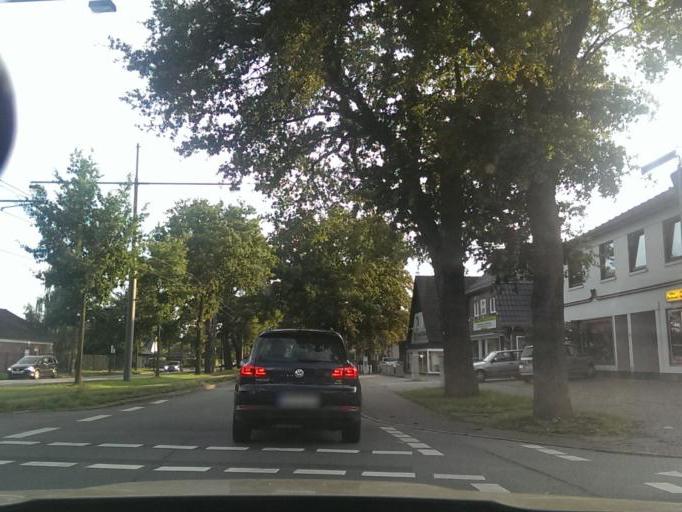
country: DE
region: Lower Saxony
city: Lilienthal
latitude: 53.1184
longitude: 8.8968
